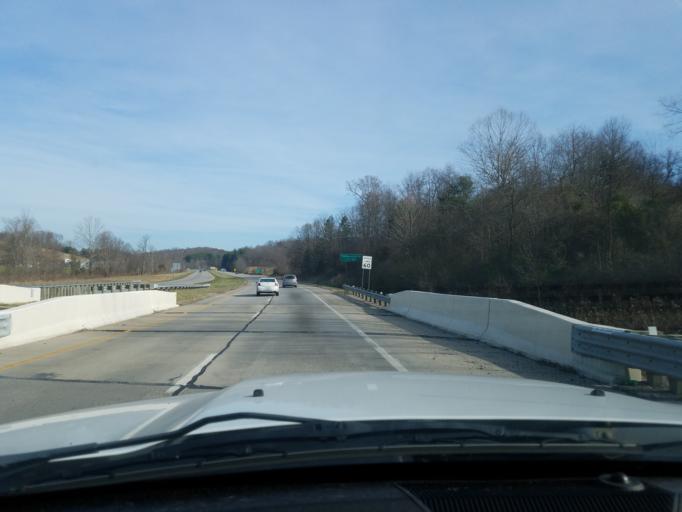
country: US
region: Ohio
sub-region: Jackson County
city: Jackson
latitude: 39.0502
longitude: -82.6001
